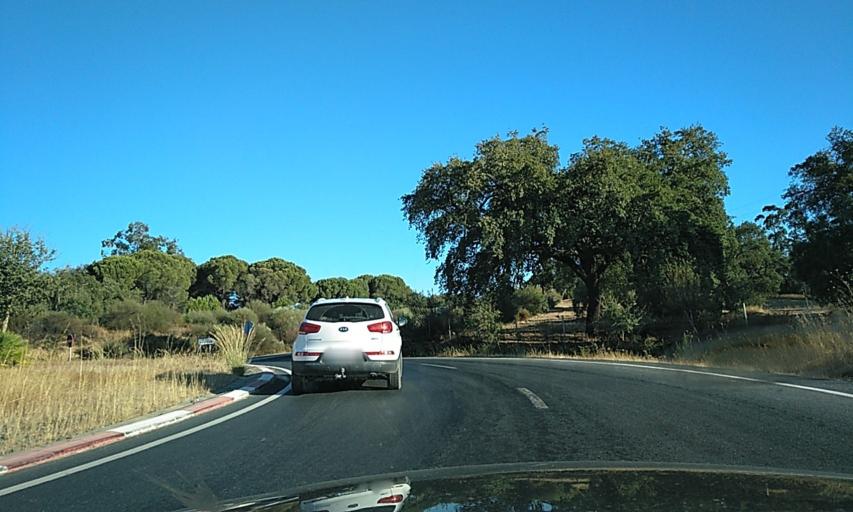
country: ES
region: Andalusia
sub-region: Provincia de Huelva
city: San Bartolome de la Torre
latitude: 37.4325
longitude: -7.1080
